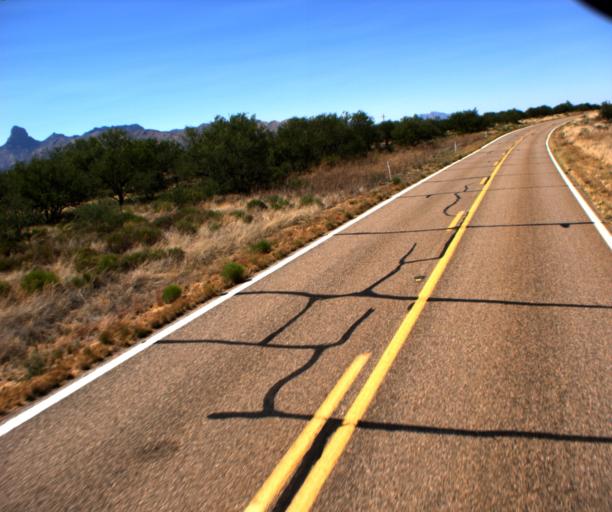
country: US
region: Arizona
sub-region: Pima County
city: Arivaca Junction
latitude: 31.6745
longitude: -111.4877
